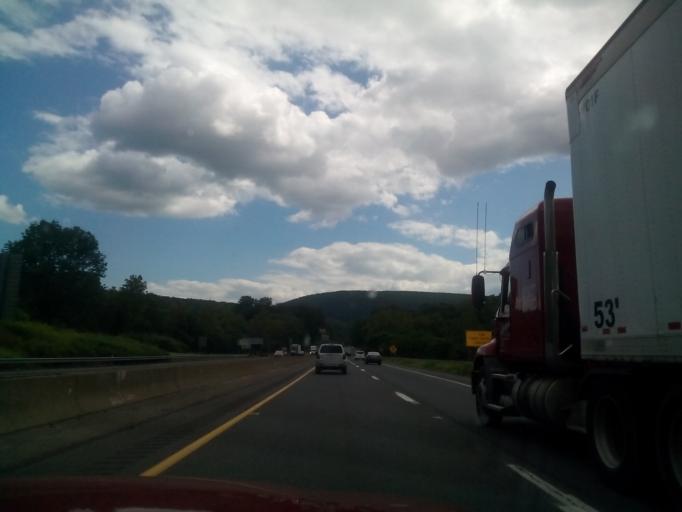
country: US
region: Pennsylvania
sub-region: Monroe County
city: East Stroudsburg
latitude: 40.9891
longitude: -75.1401
